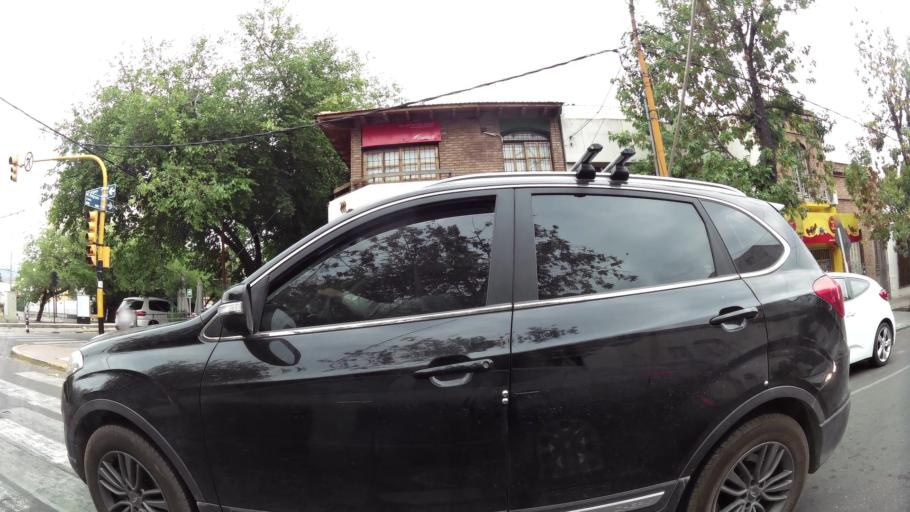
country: AR
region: Mendoza
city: Mendoza
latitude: -32.8895
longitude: -68.8530
